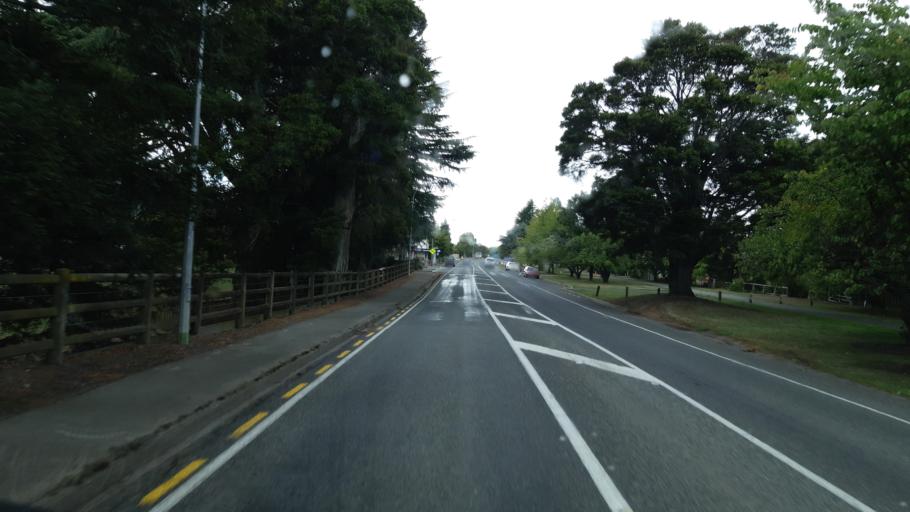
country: NZ
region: Tasman
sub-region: Tasman District
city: Wakefield
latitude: -41.4069
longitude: 173.0402
